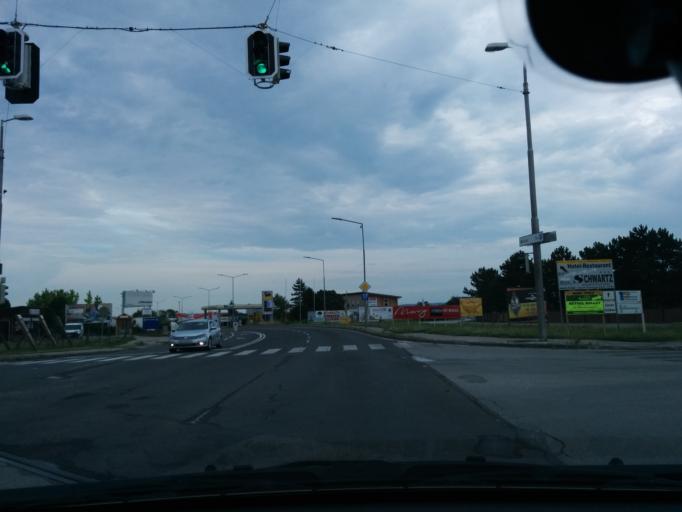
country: AT
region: Lower Austria
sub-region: Politischer Bezirk Neunkirchen
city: Neunkirchen
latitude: 47.7282
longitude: 16.0909
